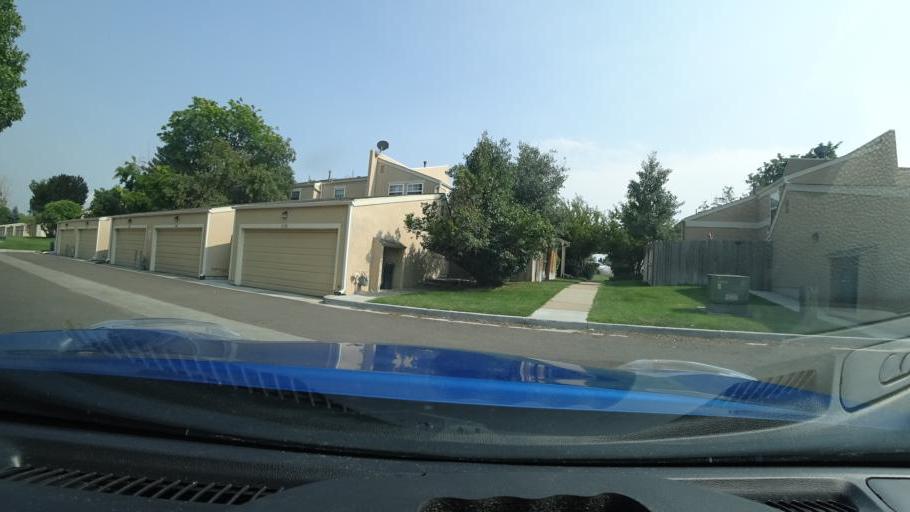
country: US
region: Colorado
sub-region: Adams County
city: Aurora
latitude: 39.6668
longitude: -104.8376
